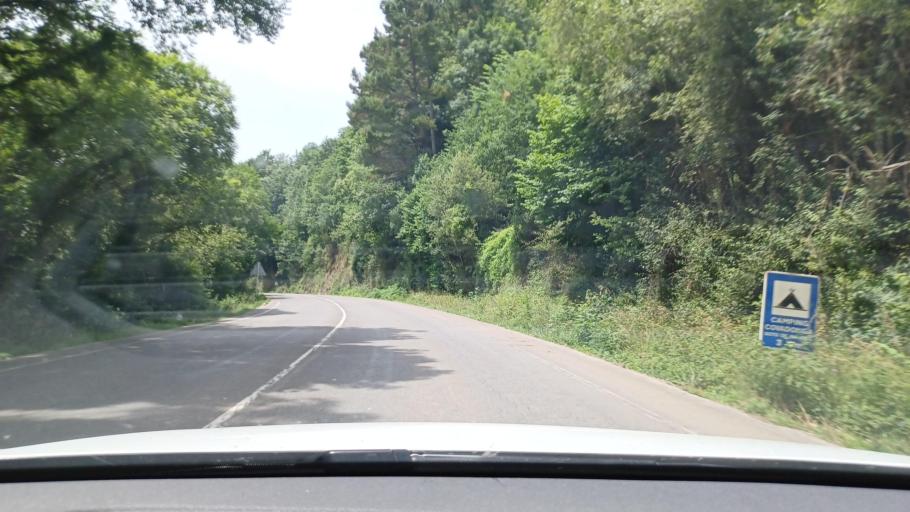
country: ES
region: Asturias
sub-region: Province of Asturias
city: Cangas de Onis
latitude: 43.3477
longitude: -5.0533
